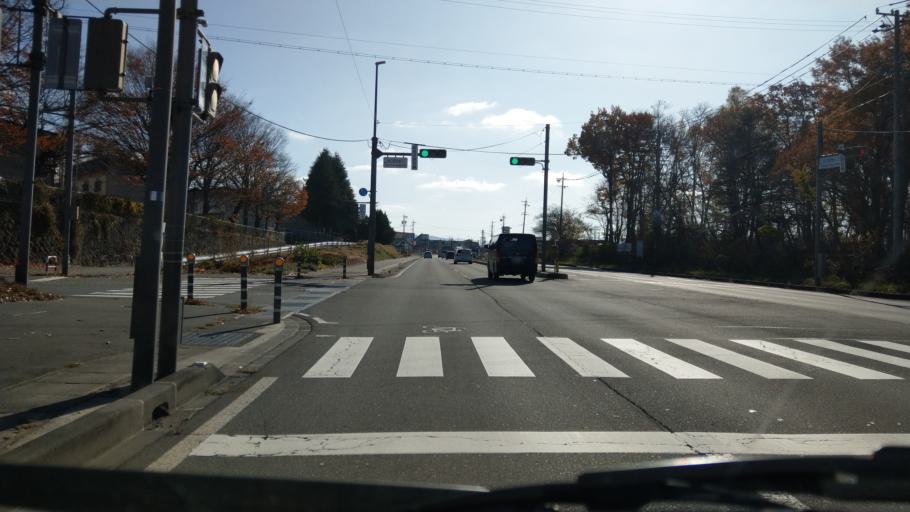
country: JP
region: Nagano
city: Komoro
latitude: 36.3031
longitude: 138.4635
